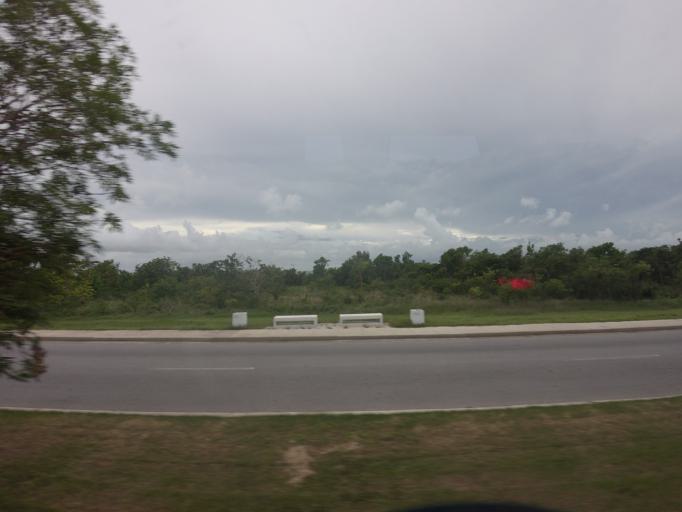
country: CU
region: Matanzas
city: Varadero
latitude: 23.1936
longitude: -81.1517
